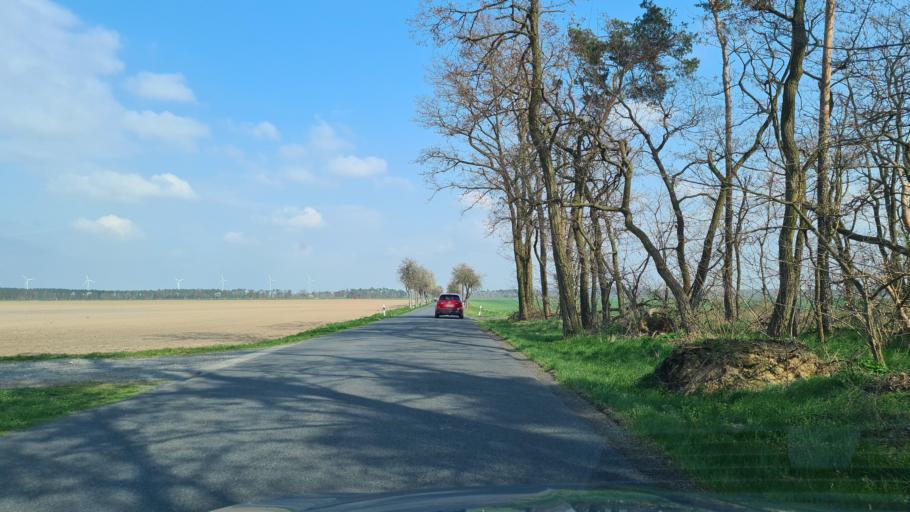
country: DE
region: Saxony
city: Nauwalde
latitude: 51.4126
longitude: 13.4679
